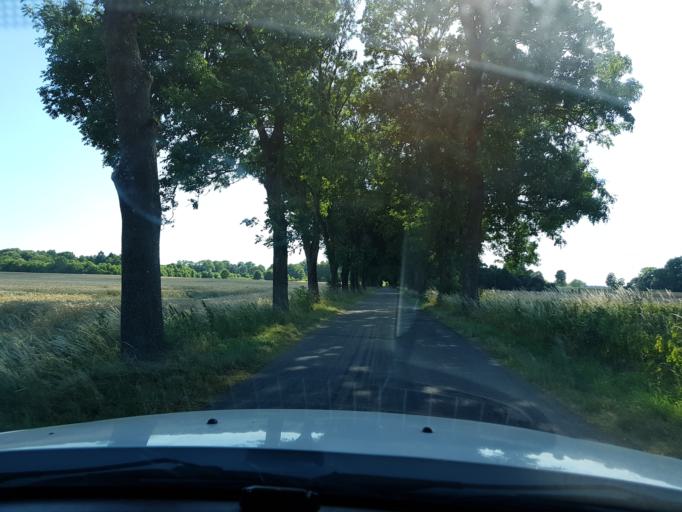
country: PL
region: West Pomeranian Voivodeship
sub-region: Powiat swidwinski
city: Slawoborze
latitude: 53.8493
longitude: 15.7148
